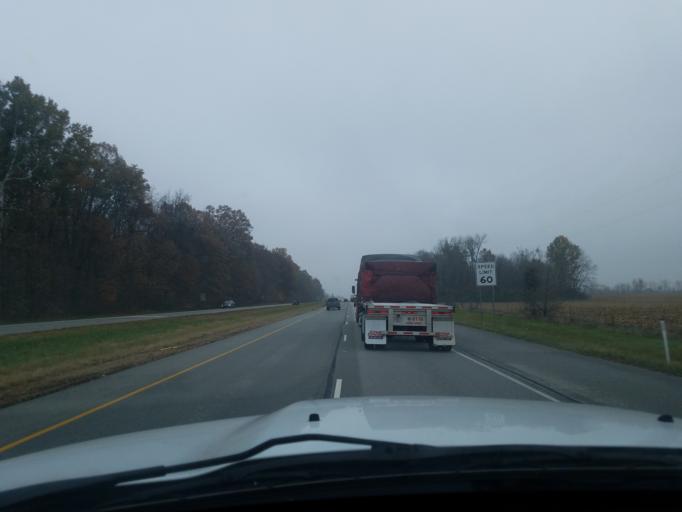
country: US
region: Indiana
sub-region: Hamilton County
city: Westfield
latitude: 40.1026
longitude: -86.1278
